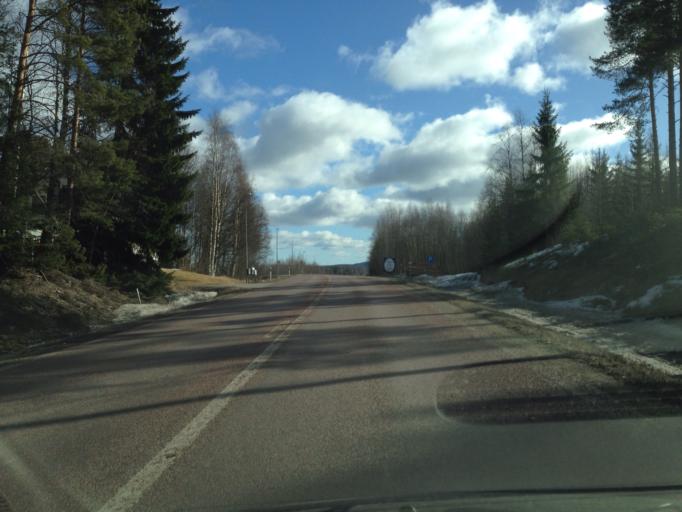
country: SE
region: Gaevleborg
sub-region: Ljusdals Kommun
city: Farila
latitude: 61.8000
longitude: 15.8031
